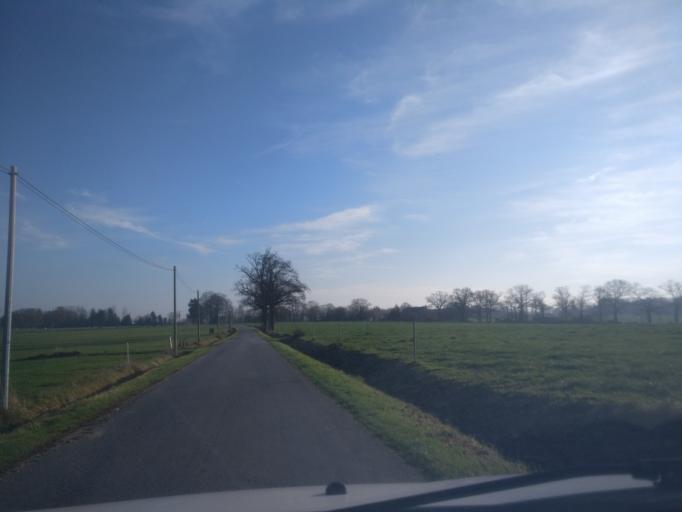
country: FR
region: Brittany
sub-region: Departement d'Ille-et-Vilaine
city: Montreuil-sous-Perouse
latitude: 48.2006
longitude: -1.2794
